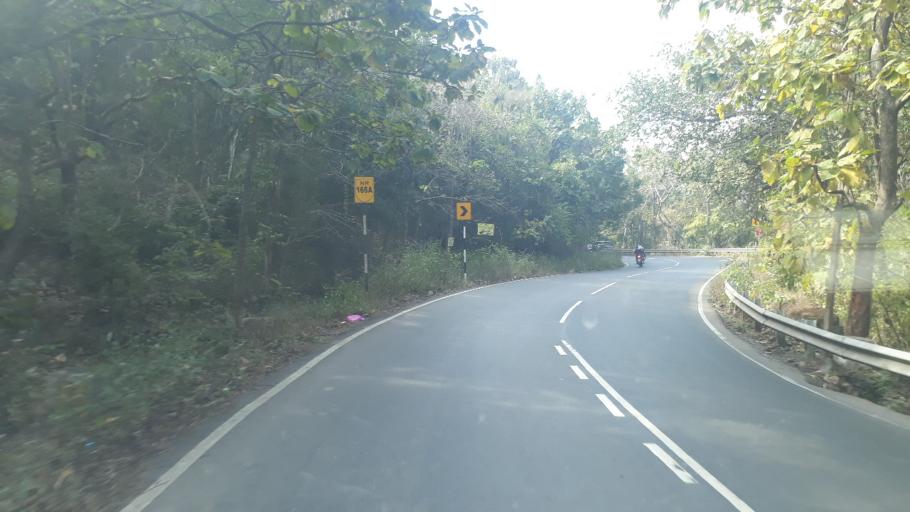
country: IN
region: Maharashtra
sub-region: Raigarh
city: Alibag
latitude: 18.6960
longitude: 72.9289
